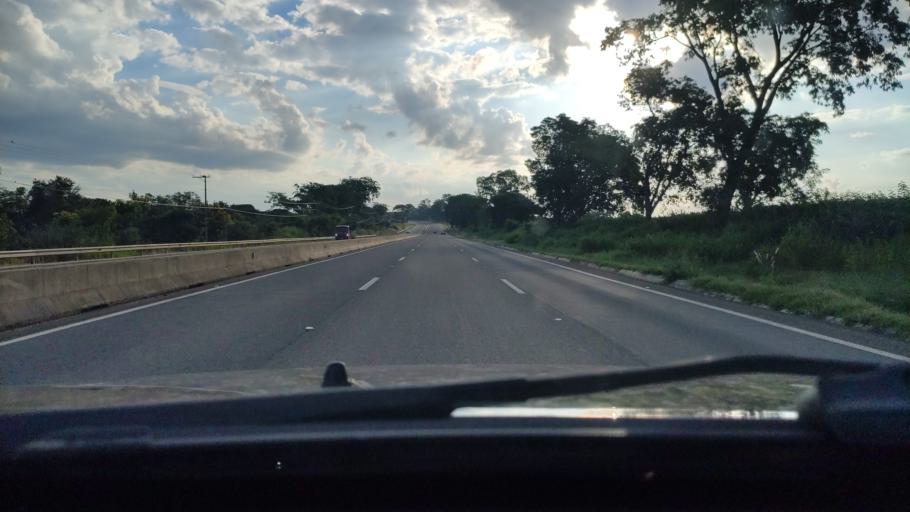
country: BR
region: Sao Paulo
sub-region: Mogi-Mirim
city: Mogi Mirim
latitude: -22.4505
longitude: -47.0762
